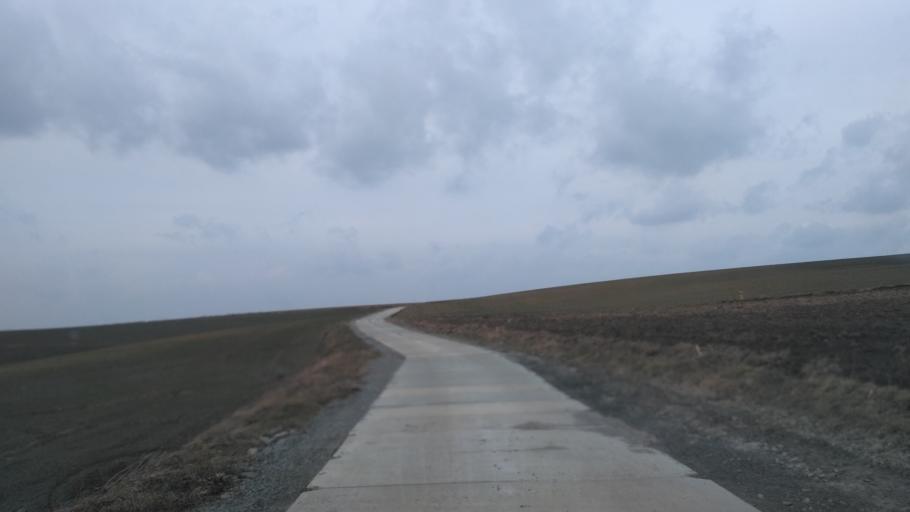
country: PL
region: Subcarpathian Voivodeship
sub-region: Powiat jaroslawski
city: Rokietnica
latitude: 49.9270
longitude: 22.5954
